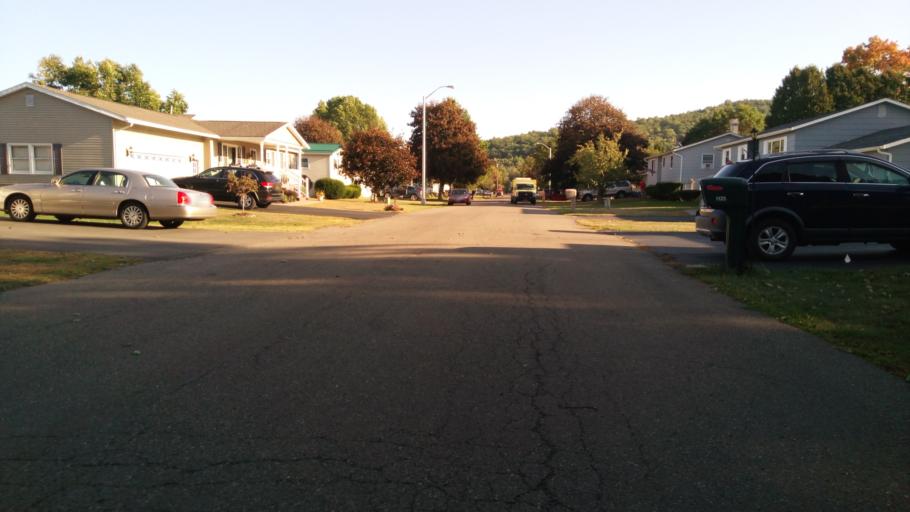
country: US
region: New York
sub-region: Chemung County
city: Southport
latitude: 42.0560
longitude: -76.8359
